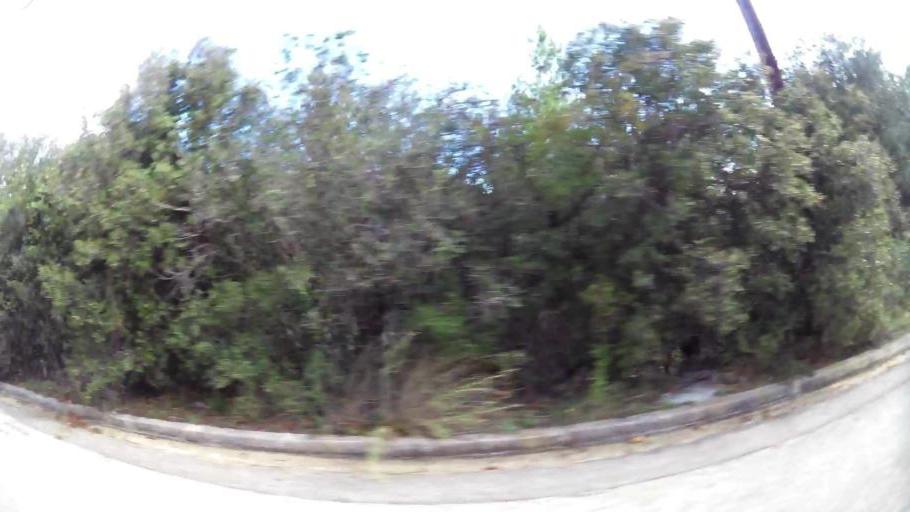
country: GR
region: Attica
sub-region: Nomarchia Anatolikis Attikis
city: Thrakomakedones
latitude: 38.1441
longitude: 23.7579
